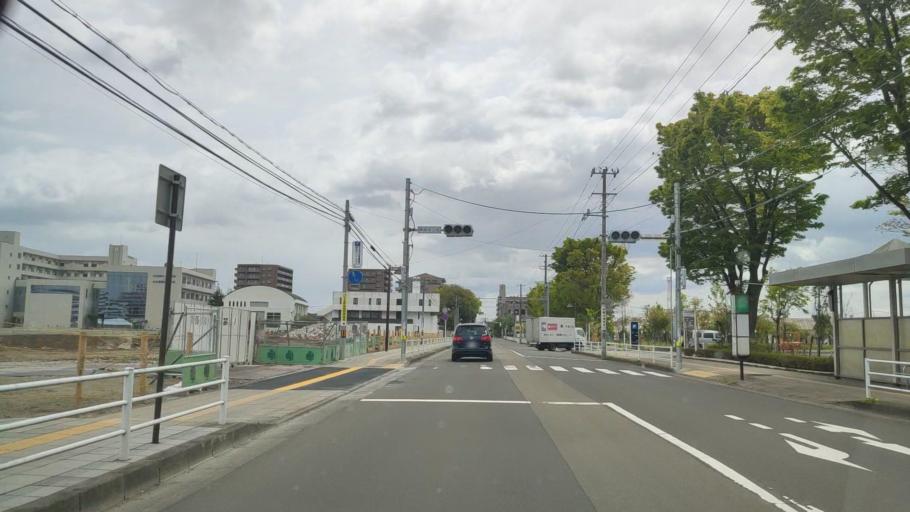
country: JP
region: Miyagi
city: Sendai-shi
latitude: 38.2608
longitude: 140.9062
